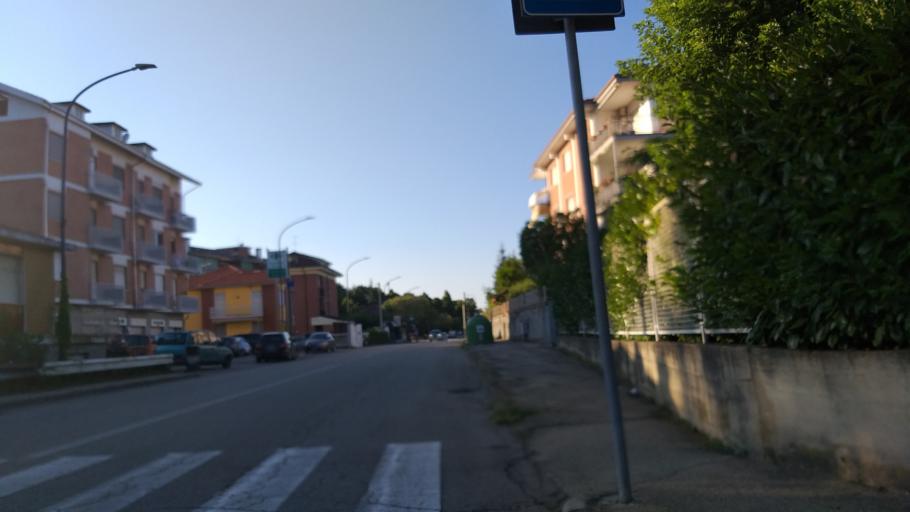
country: IT
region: Piedmont
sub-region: Provincia di Asti
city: Asti
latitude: 44.9104
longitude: 8.2063
